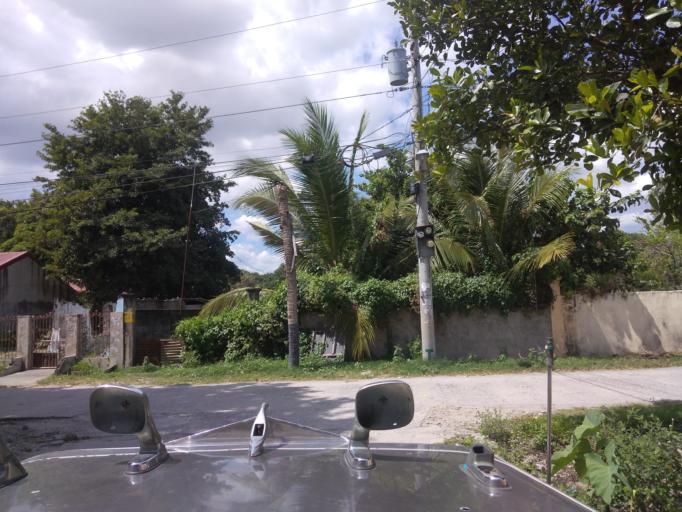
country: PH
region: Central Luzon
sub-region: Province of Pampanga
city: San Basilio
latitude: 15.0165
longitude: 120.5859
